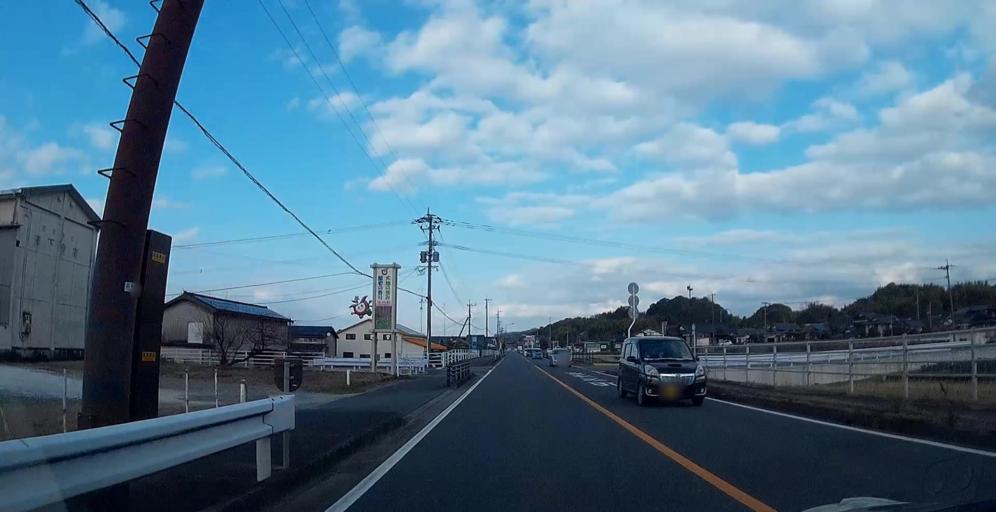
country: JP
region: Kumamoto
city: Yatsushiro
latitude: 32.5430
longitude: 130.6745
